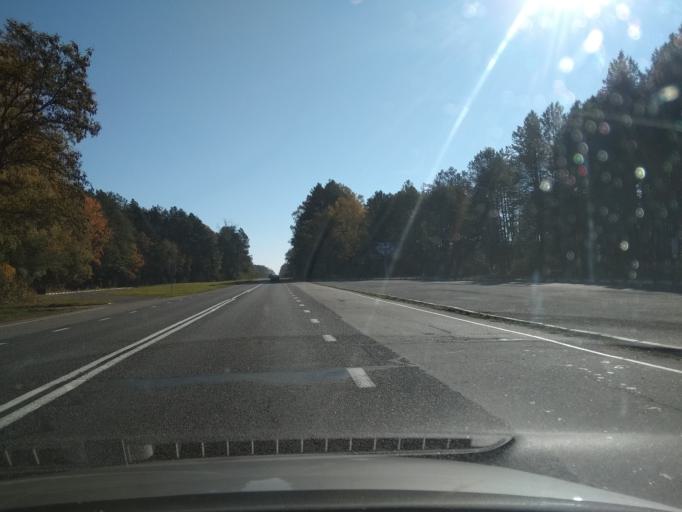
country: BY
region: Brest
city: Malaryta
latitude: 51.9222
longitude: 24.0796
